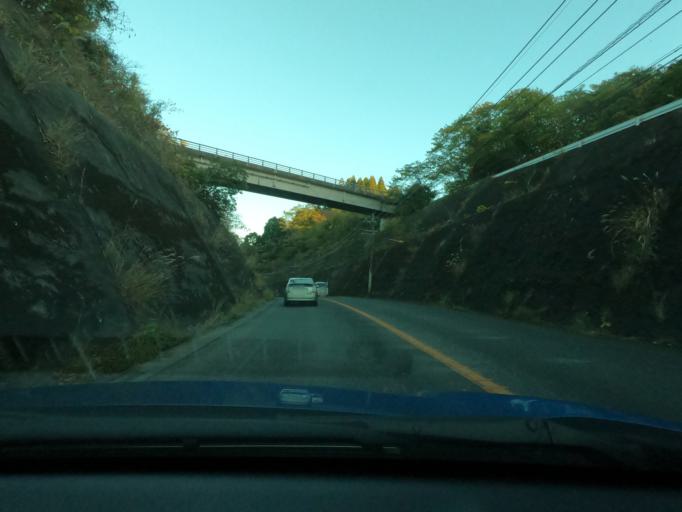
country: JP
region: Kagoshima
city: Satsumasendai
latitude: 31.7961
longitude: 130.4217
